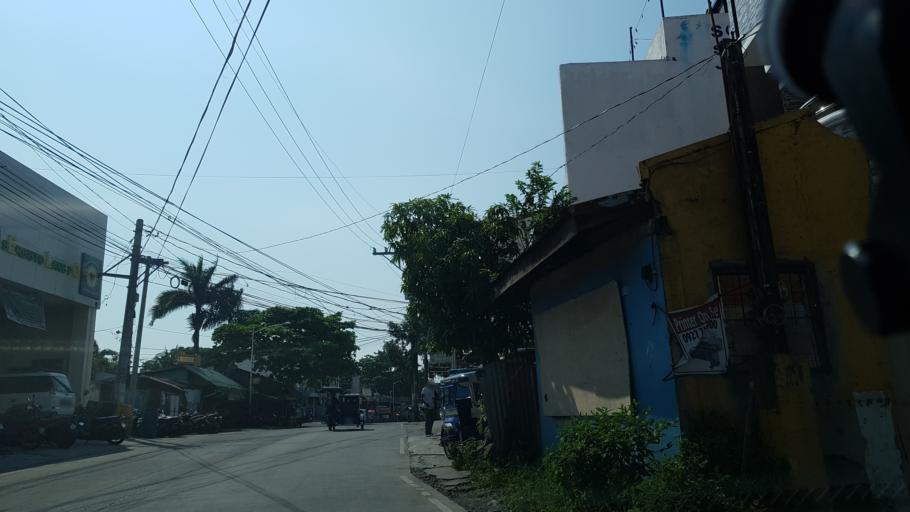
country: PH
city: Sambayanihan People's Village
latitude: 14.4875
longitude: 121.0250
